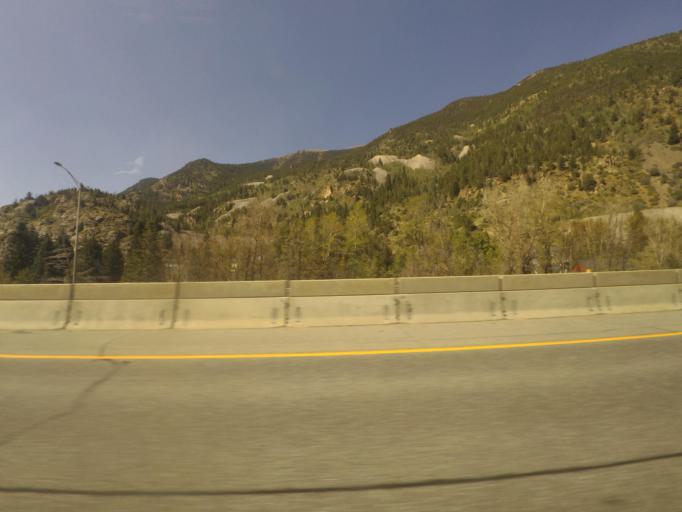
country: US
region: Colorado
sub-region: Clear Creek County
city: Georgetown
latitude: 39.6975
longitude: -105.7239
